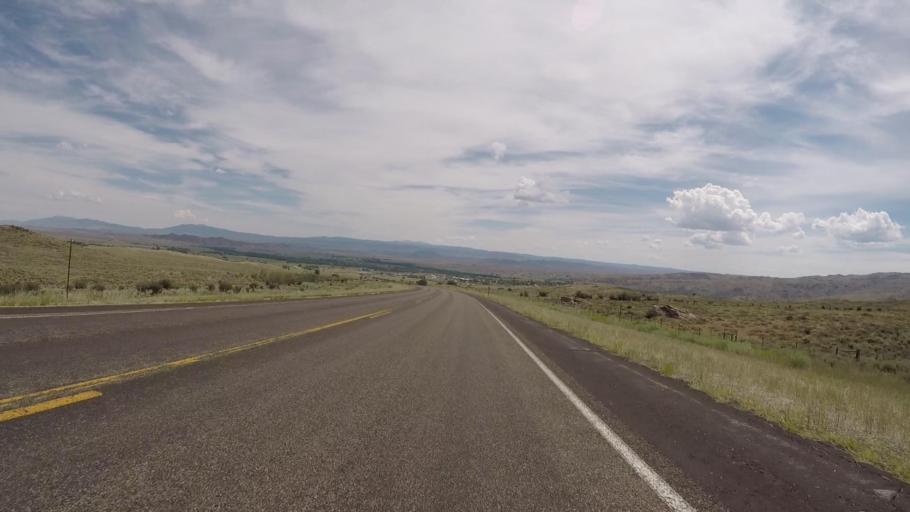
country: US
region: Wyoming
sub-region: Carbon County
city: Saratoga
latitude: 41.2038
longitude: -106.8219
